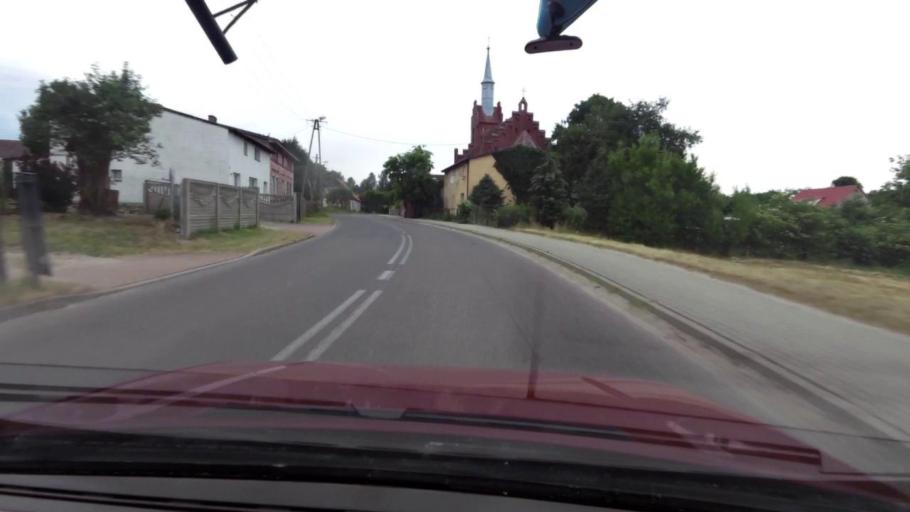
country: PL
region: West Pomeranian Voivodeship
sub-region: Powiat koszalinski
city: Sianow
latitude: 54.1796
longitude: 16.3837
